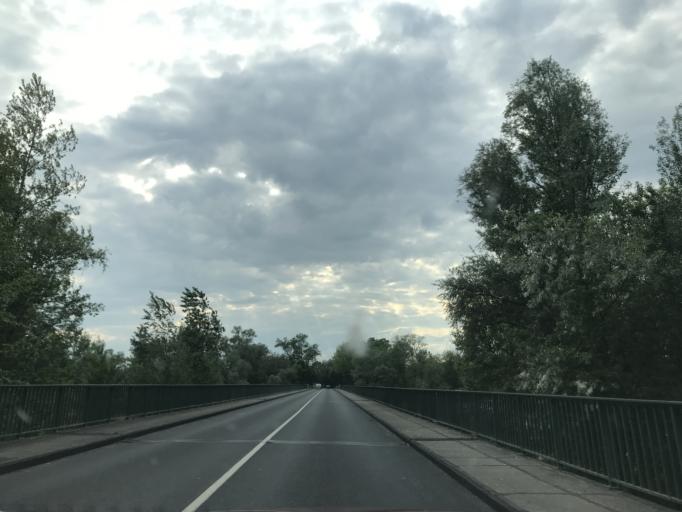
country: FR
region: Auvergne
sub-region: Departement du Puy-de-Dome
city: Maringues
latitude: 45.9164
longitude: 3.3656
